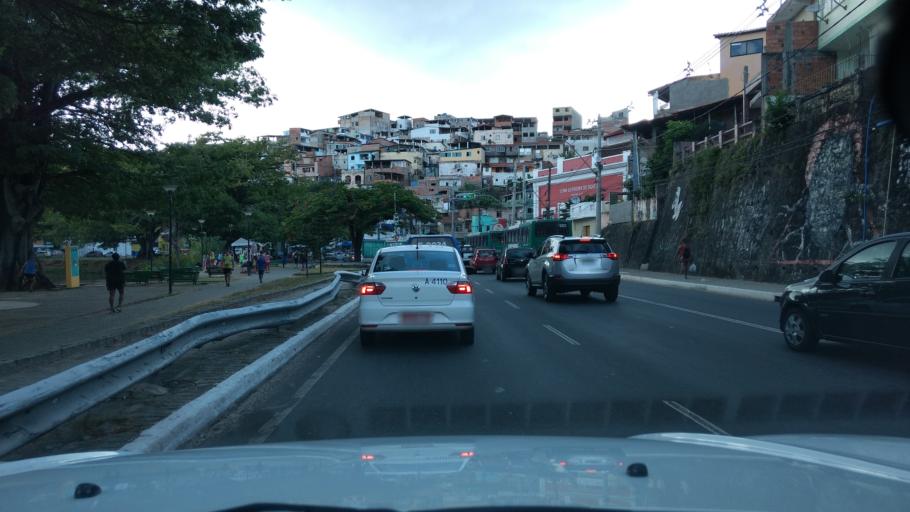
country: BR
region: Bahia
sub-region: Salvador
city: Salvador
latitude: -12.9851
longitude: -38.5056
